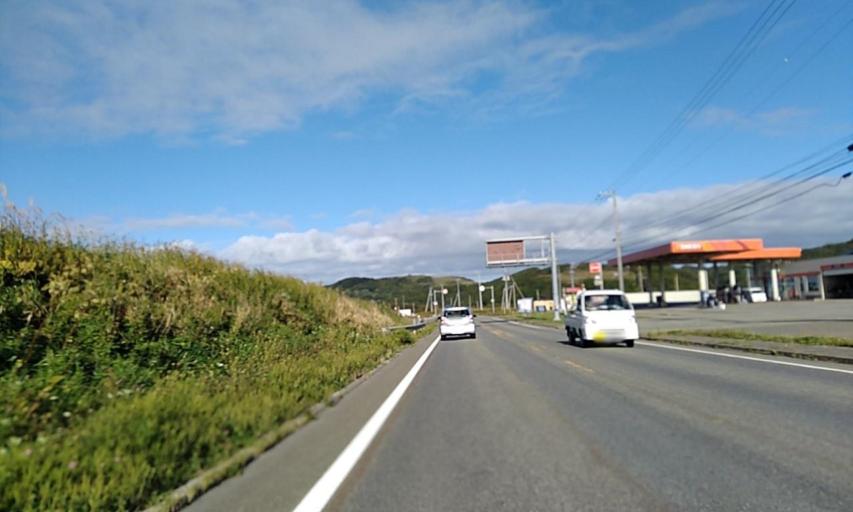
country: JP
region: Hokkaido
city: Shizunai-furukawacho
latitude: 42.1853
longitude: 142.7239
